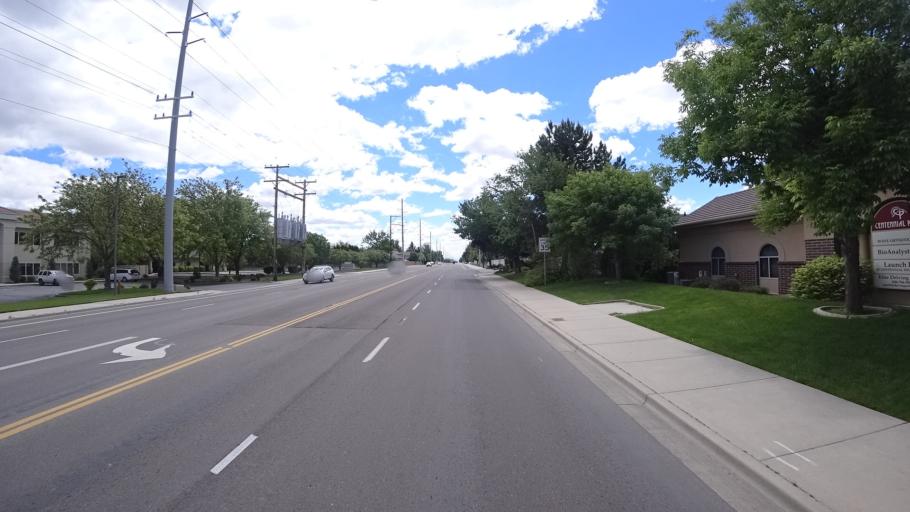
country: US
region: Idaho
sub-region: Ada County
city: Eagle
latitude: 43.6478
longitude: -116.3344
